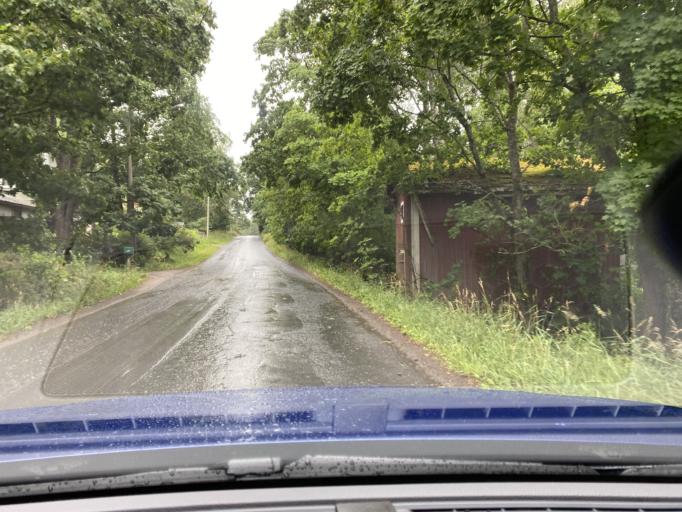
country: FI
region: Pirkanmaa
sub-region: Lounais-Pirkanmaa
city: Punkalaidun
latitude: 61.1483
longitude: 23.1903
